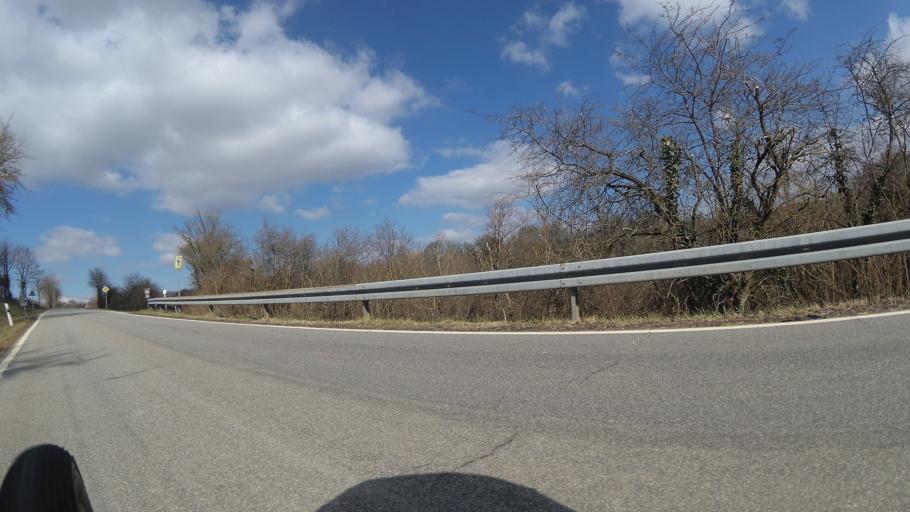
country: DE
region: Saarland
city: Rehlingen-Siersburg
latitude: 49.3649
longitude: 6.6077
